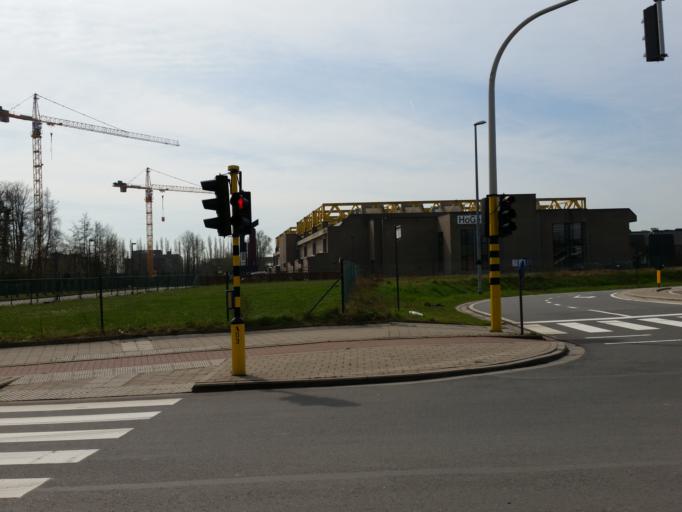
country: BE
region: Flanders
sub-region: Provincie Oost-Vlaanderen
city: Gent
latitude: 51.0361
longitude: 3.7047
